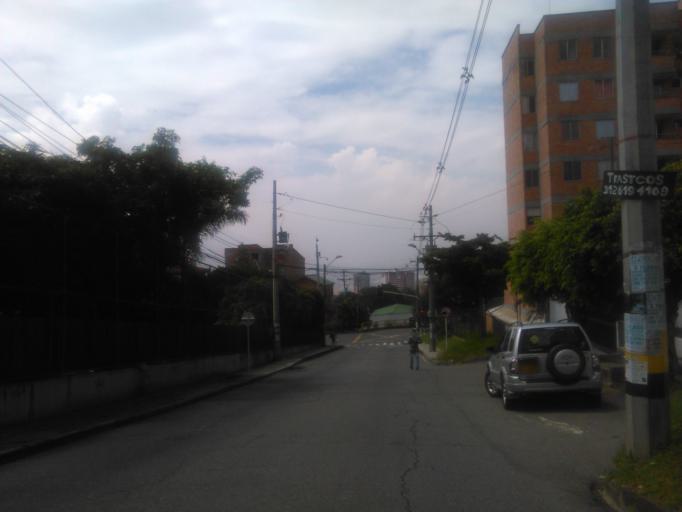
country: CO
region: Antioquia
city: Medellin
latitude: 6.2804
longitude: -75.5879
